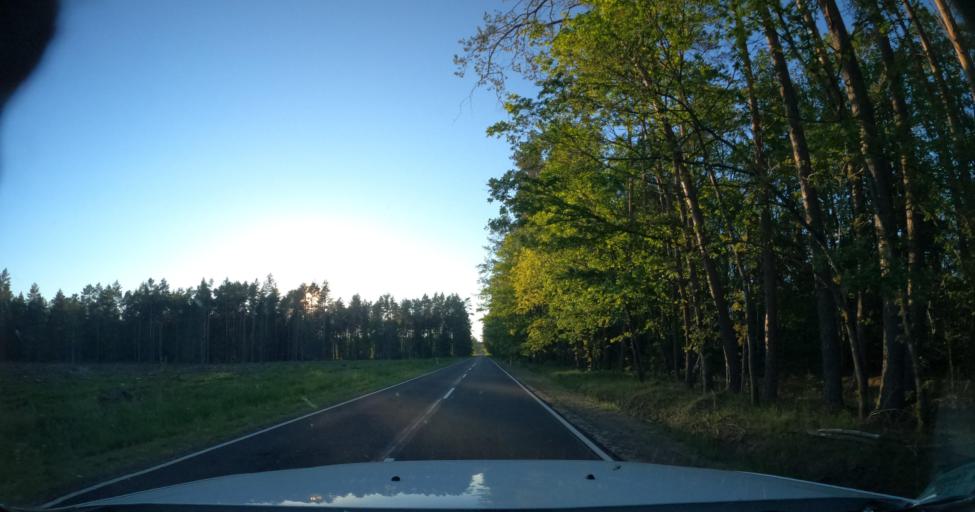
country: PL
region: Pomeranian Voivodeship
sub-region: Powiat bytowski
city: Czarna Dabrowka
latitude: 54.3859
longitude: 17.4813
